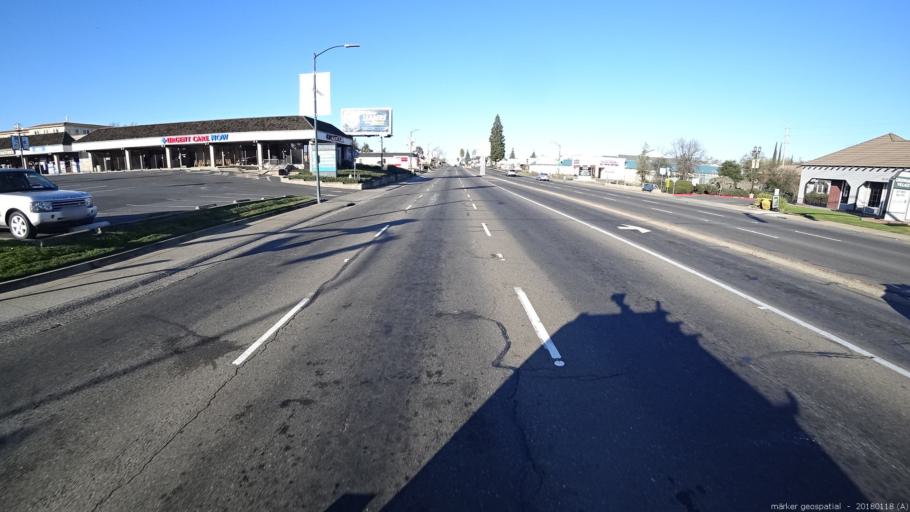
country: US
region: California
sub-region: Sacramento County
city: Citrus Heights
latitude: 38.6785
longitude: -121.2623
